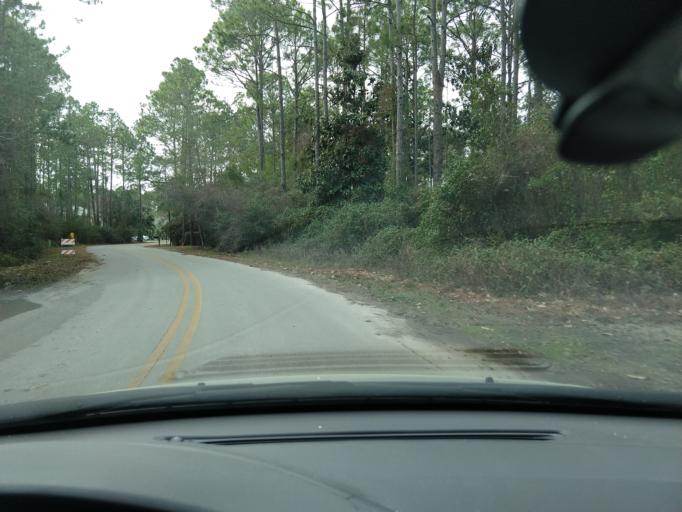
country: US
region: Florida
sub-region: Walton County
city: Seaside
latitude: 30.4015
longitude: -86.2082
